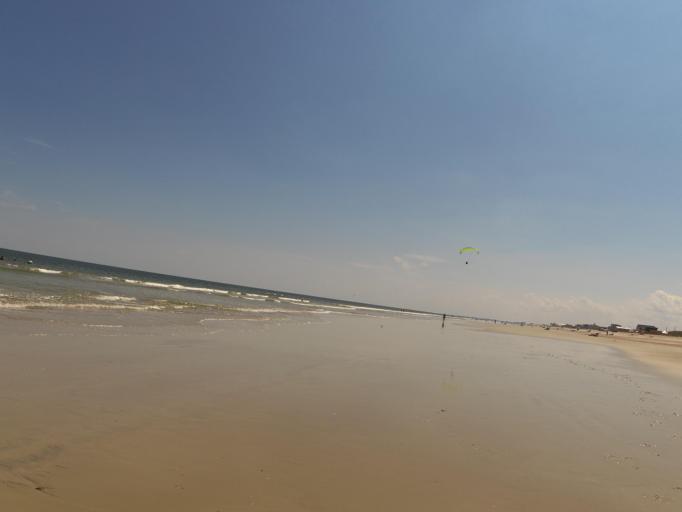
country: US
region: Florida
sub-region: Nassau County
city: Fernandina Beach
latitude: 30.6637
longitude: -81.4303
